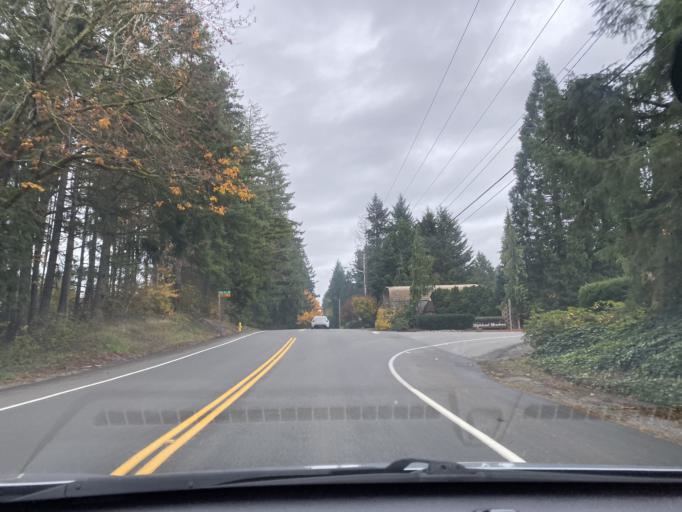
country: US
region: Washington
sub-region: King County
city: Lea Hill
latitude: 47.3007
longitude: -122.1653
